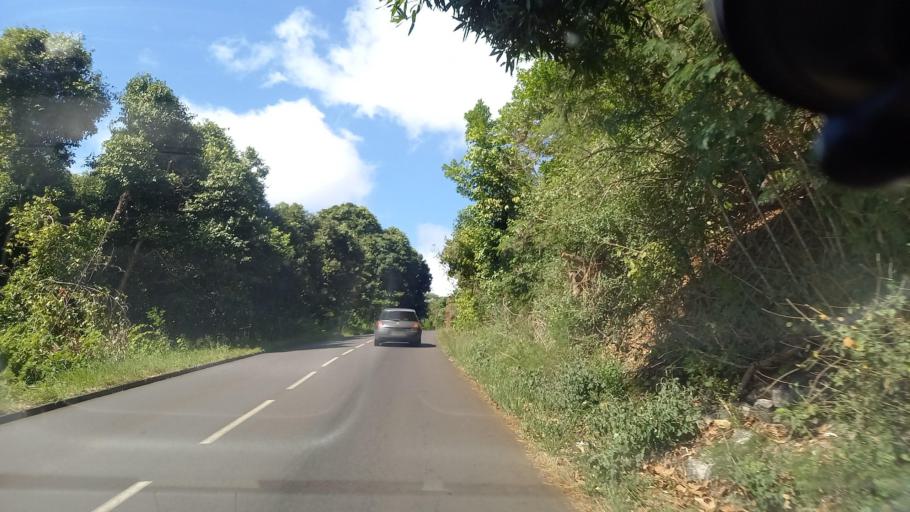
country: YT
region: Tsingoni
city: Tsingoni
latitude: -12.7849
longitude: 45.1494
